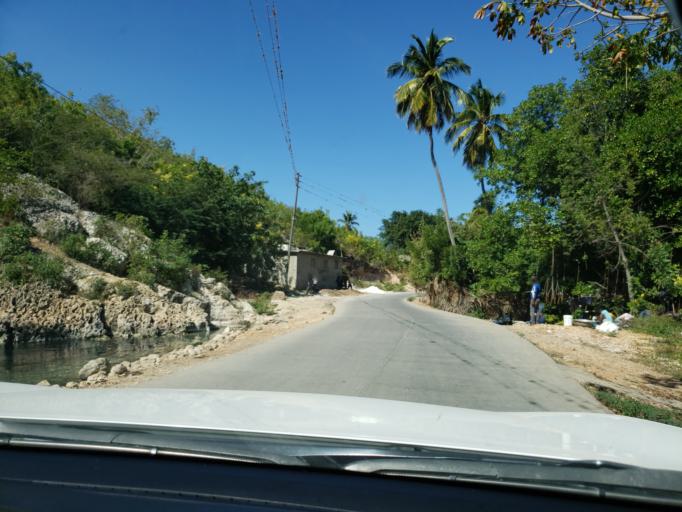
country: HT
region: Nippes
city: Miragoane
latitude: 18.4454
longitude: -73.1048
